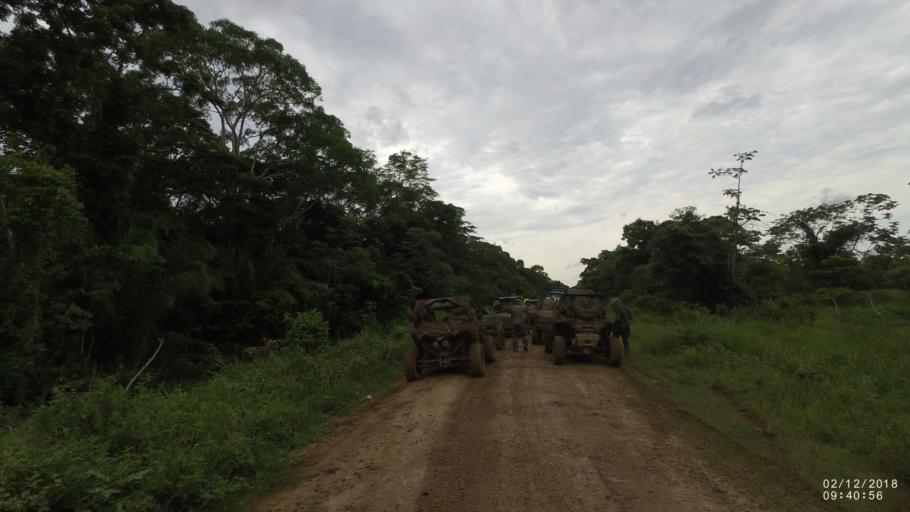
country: BO
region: Santa Cruz
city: Ascension
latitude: -15.8680
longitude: -63.5825
